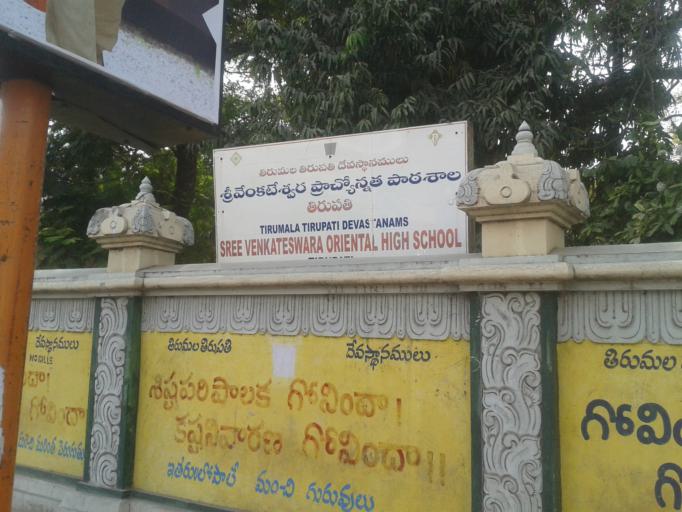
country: IN
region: Andhra Pradesh
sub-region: Chittoor
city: Tirupati
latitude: 13.6395
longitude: 79.4187
